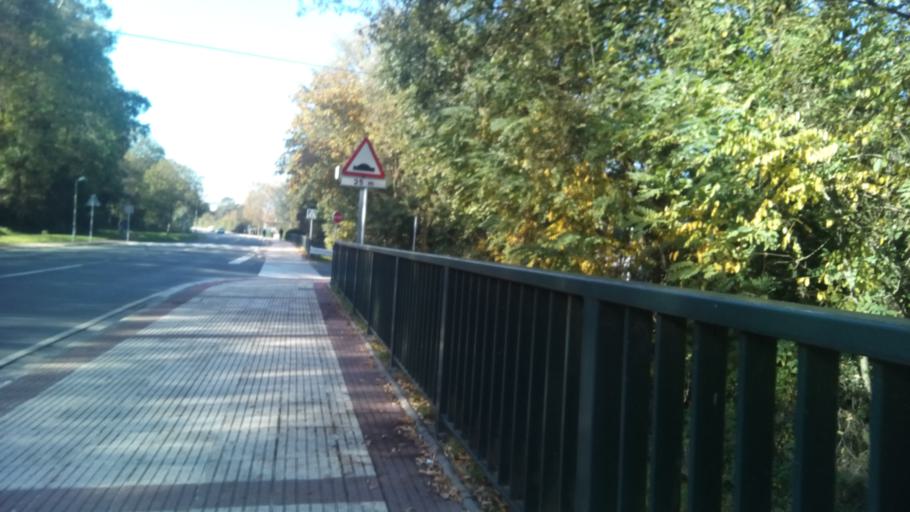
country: ES
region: Basque Country
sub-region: Bizkaia
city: Zamudio
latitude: 43.2752
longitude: -2.8371
